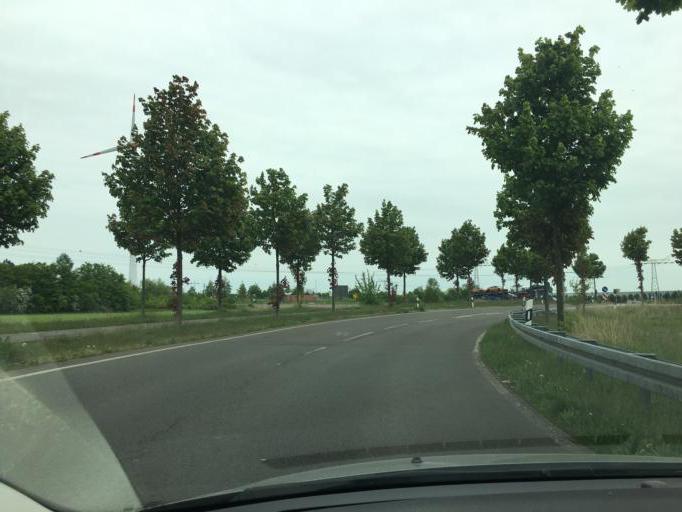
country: DE
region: Saxony
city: Rackwitz
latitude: 51.4011
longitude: 12.4269
